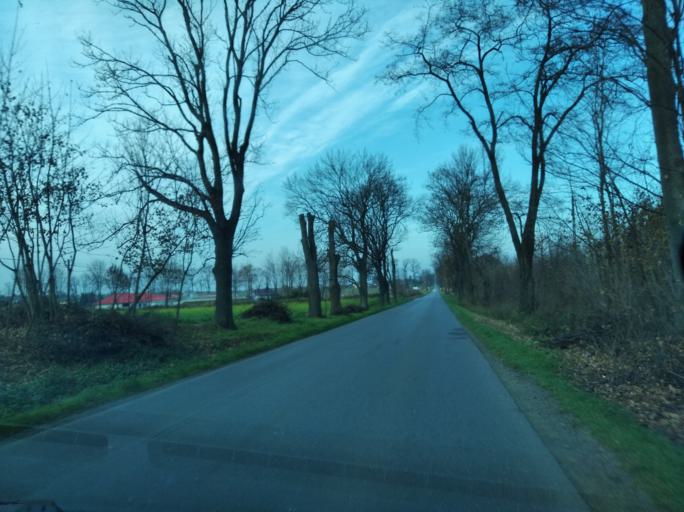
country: PL
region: Subcarpathian Voivodeship
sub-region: Powiat ropczycko-sedziszowski
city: Iwierzyce
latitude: 50.0384
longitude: 21.7461
